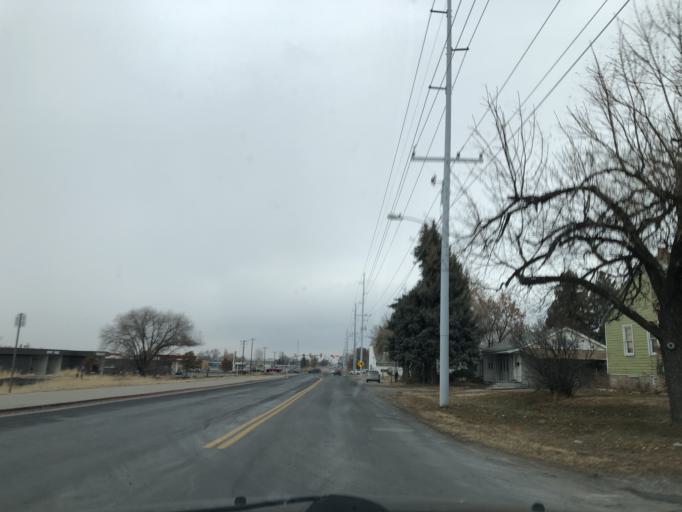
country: US
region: Utah
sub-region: Cache County
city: Logan
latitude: 41.7335
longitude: -111.8498
